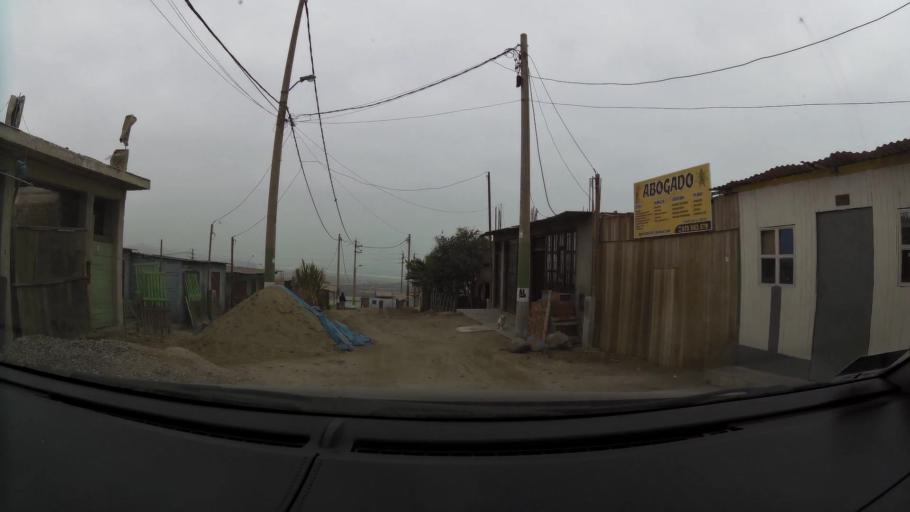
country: PE
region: Lima
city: Ventanilla
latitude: -11.8512
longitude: -77.1479
